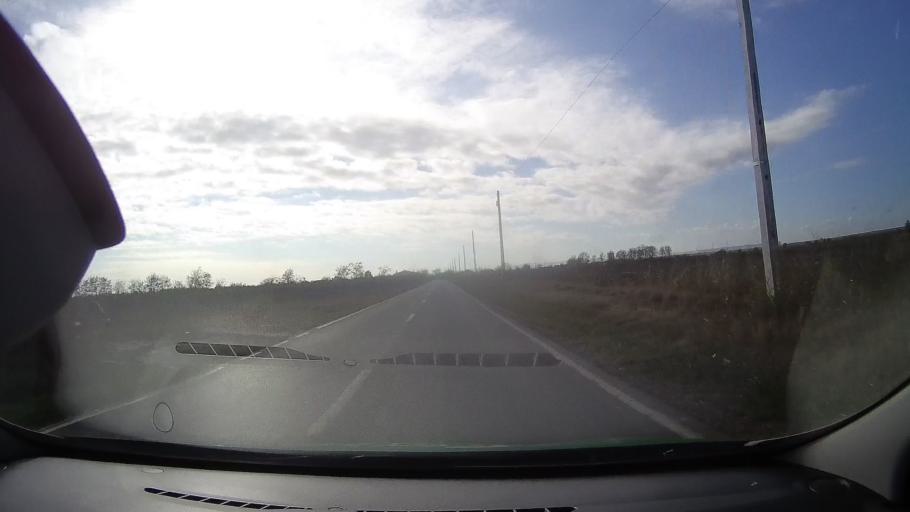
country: RO
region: Tulcea
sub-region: Comuna Sarichioi
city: Sarichioi
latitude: 44.9833
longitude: 28.8837
